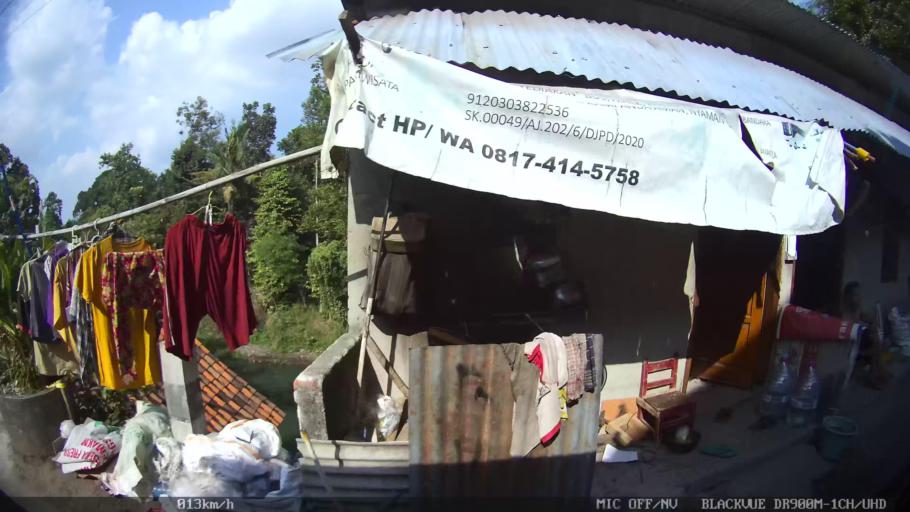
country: ID
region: Daerah Istimewa Yogyakarta
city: Sewon
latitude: -7.8339
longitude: 110.3949
